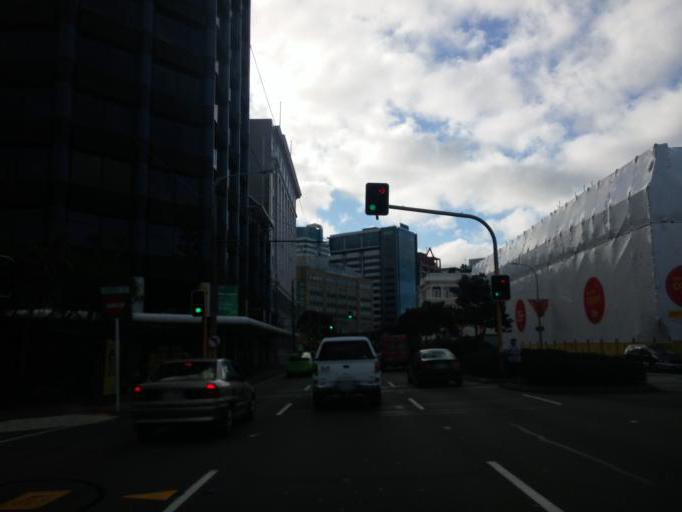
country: NZ
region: Wellington
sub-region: Wellington City
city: Wellington
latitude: -41.2858
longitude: 174.7778
